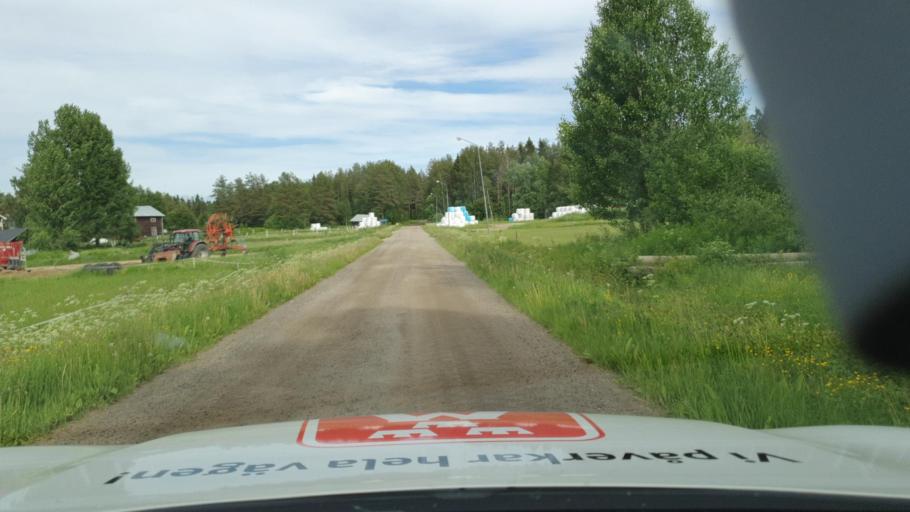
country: SE
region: Vaesterbotten
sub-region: Robertsfors Kommun
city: Robertsfors
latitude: 64.3735
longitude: 21.0593
